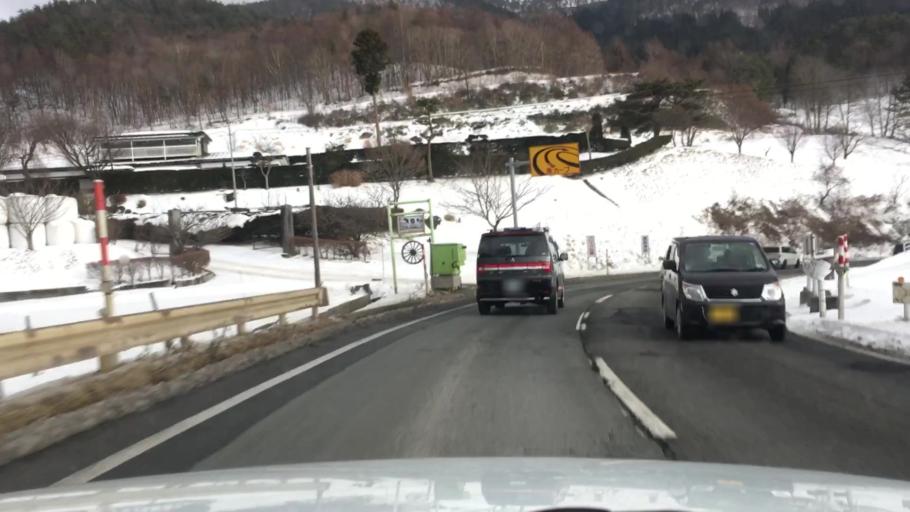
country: JP
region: Iwate
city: Morioka-shi
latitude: 39.6705
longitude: 141.3301
